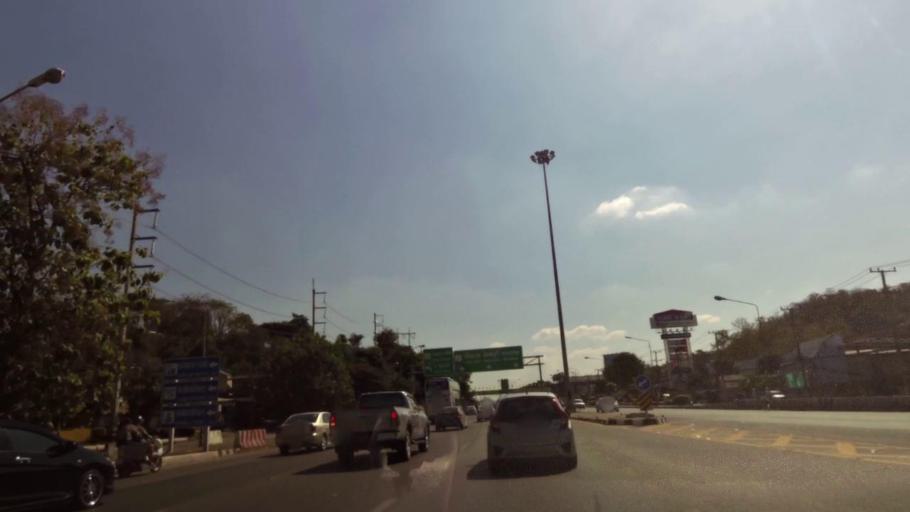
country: TH
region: Nakhon Sawan
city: Nakhon Sawan
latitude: 15.6844
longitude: 100.1243
